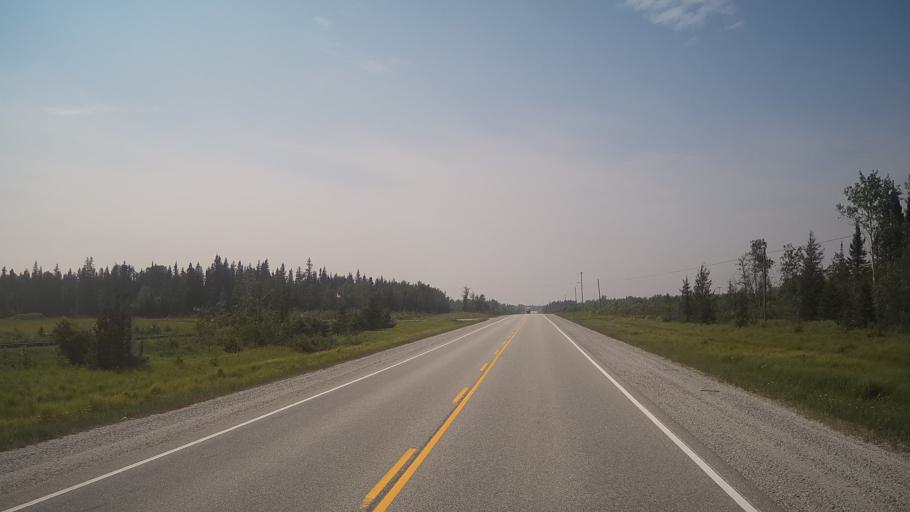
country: CA
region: Ontario
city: Kapuskasing
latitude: 49.2823
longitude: -81.7555
